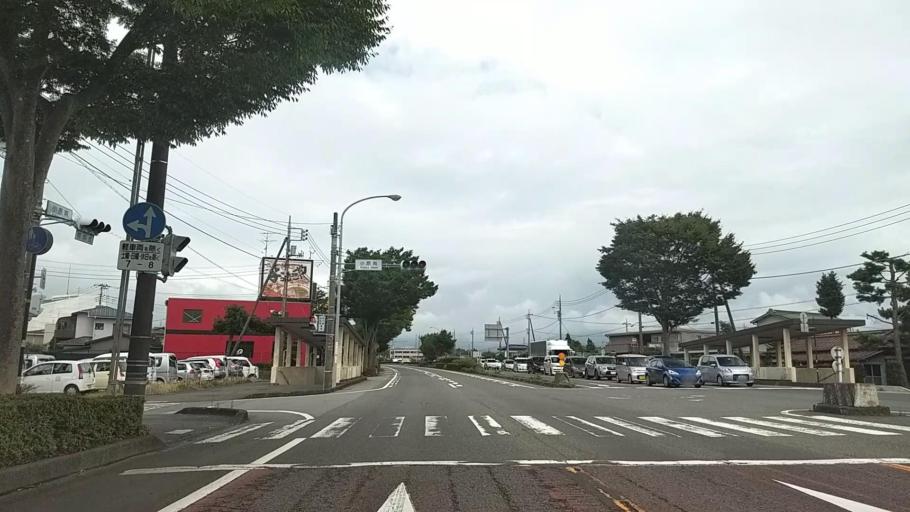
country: JP
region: Shizuoka
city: Gotemba
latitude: 35.3098
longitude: 138.9346
